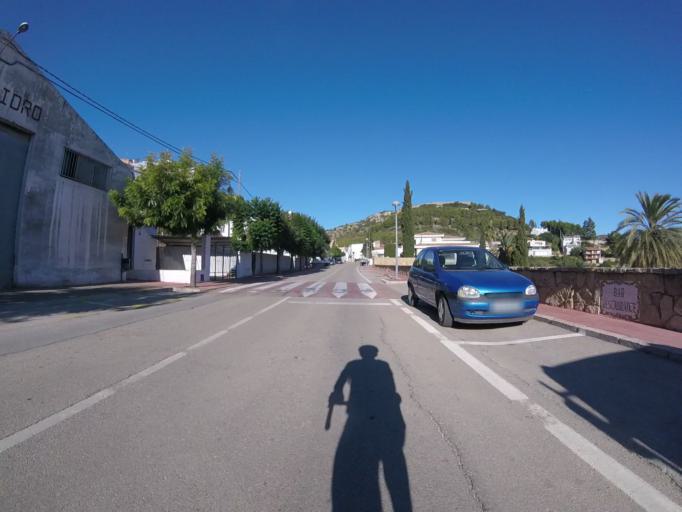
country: ES
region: Valencia
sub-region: Provincia de Castello
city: Cervera del Maestre
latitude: 40.4555
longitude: 0.2757
